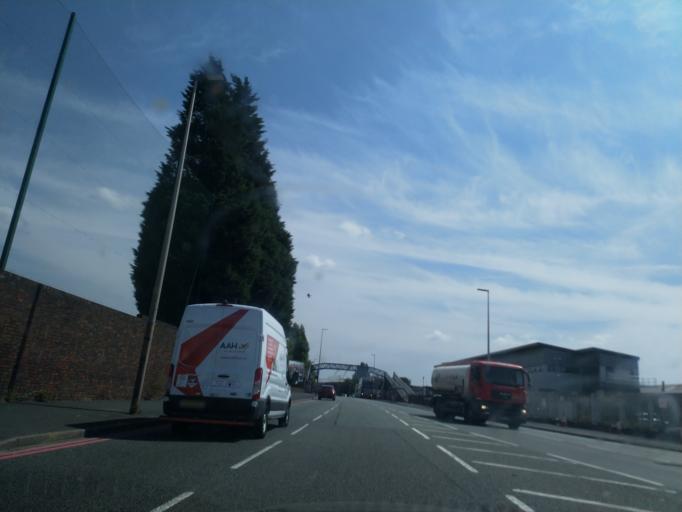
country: GB
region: England
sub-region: Sandwell
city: Smethwick
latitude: 52.5115
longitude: -1.9731
